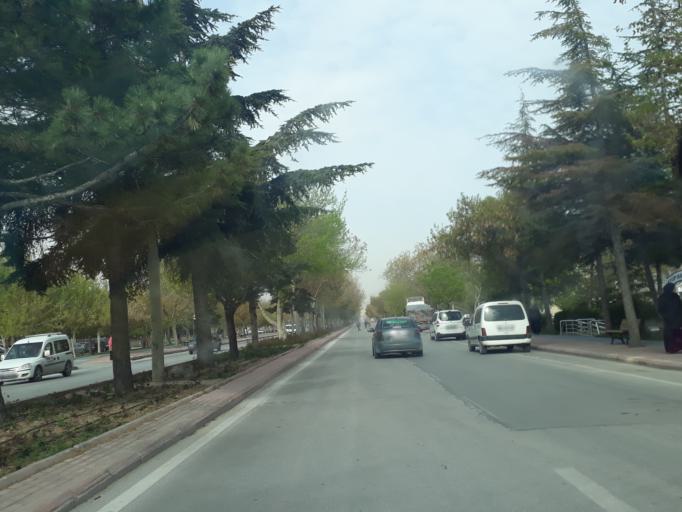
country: TR
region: Konya
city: Selcuklu
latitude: 37.9372
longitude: 32.5088
